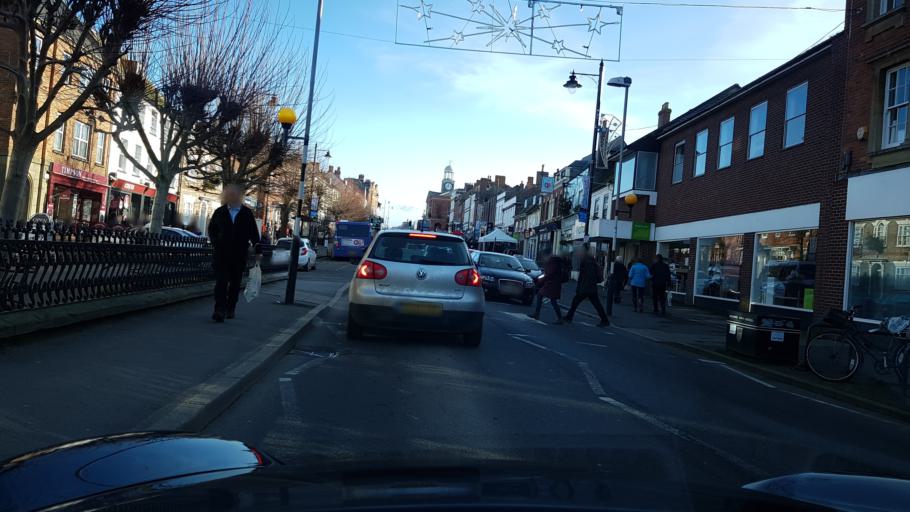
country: GB
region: England
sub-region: Dorset
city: Bridport
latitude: 50.7340
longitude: -2.7609
